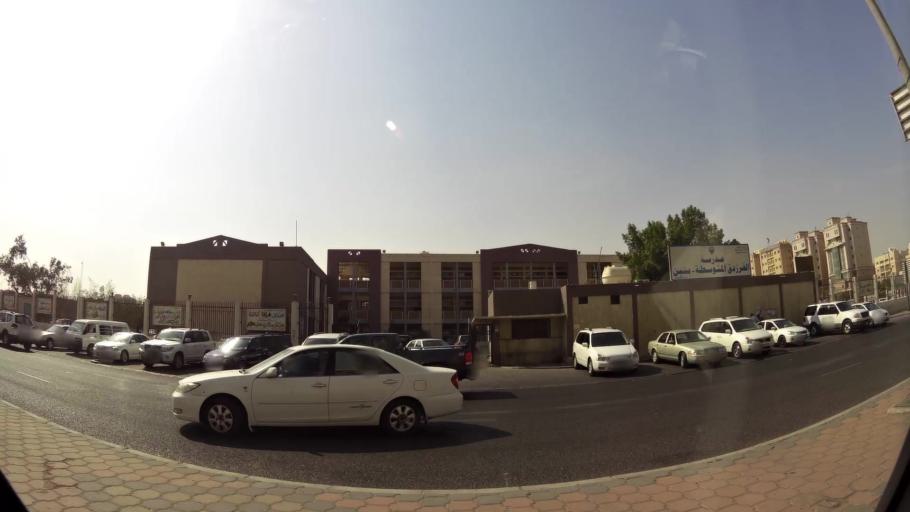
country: KW
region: Al Ahmadi
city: Al Manqaf
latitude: 29.0908
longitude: 48.1302
